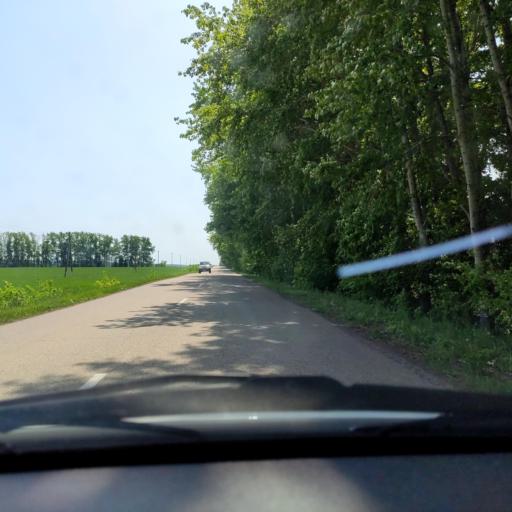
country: RU
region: Bashkortostan
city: Avdon
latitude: 54.5158
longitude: 55.6289
